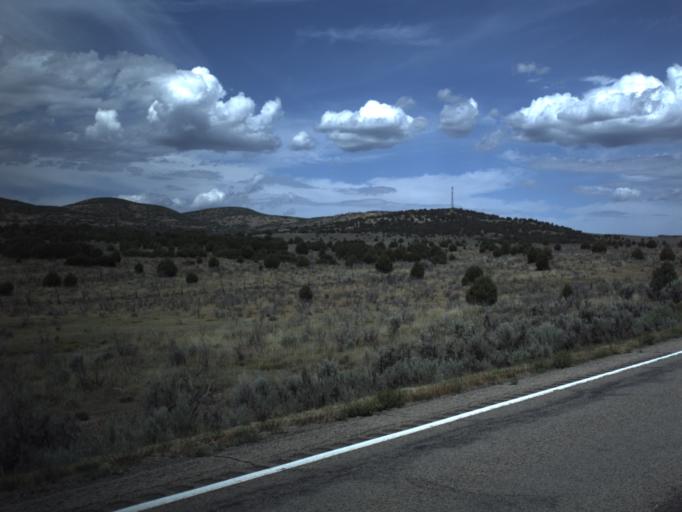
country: US
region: Utah
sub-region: Sanpete County
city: Fairview
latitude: 39.6753
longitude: -111.4565
